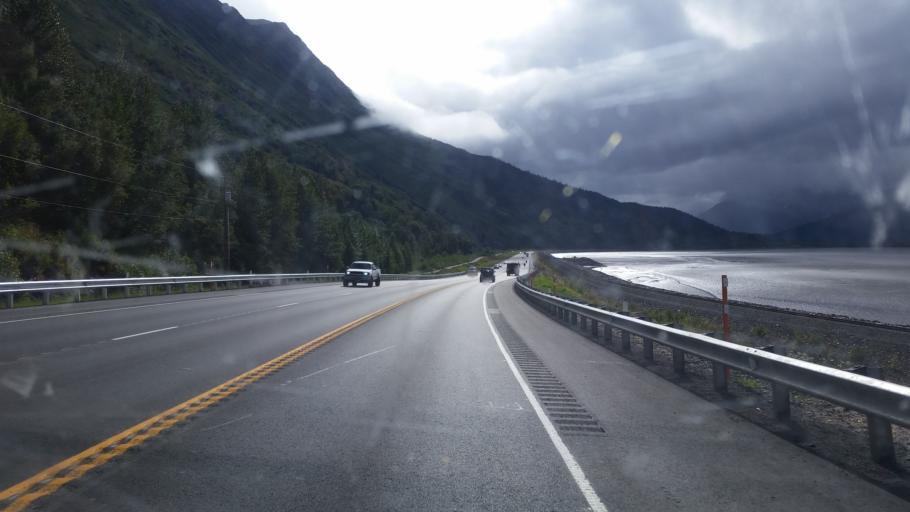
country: US
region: Alaska
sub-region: Anchorage Municipality
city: Girdwood
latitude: 60.9519
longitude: -149.4070
